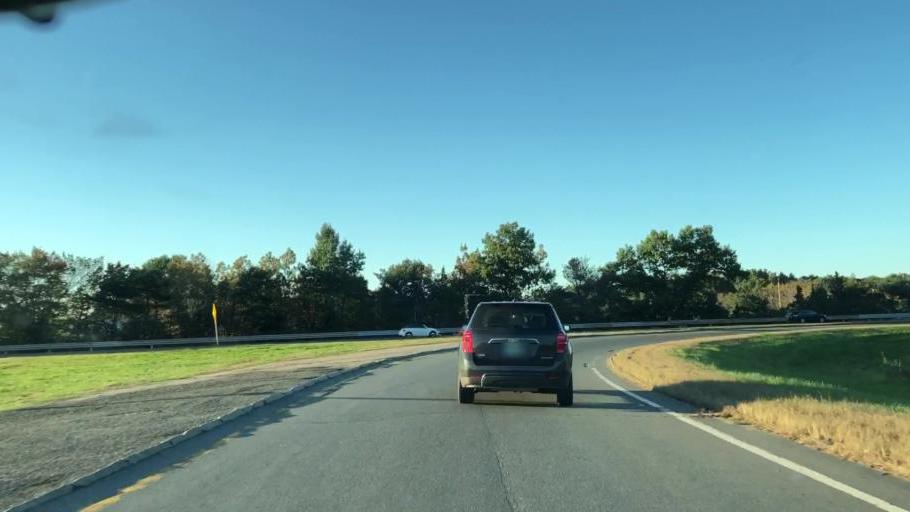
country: US
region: Massachusetts
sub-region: Essex County
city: Lawrence
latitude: 42.6647
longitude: -71.1918
